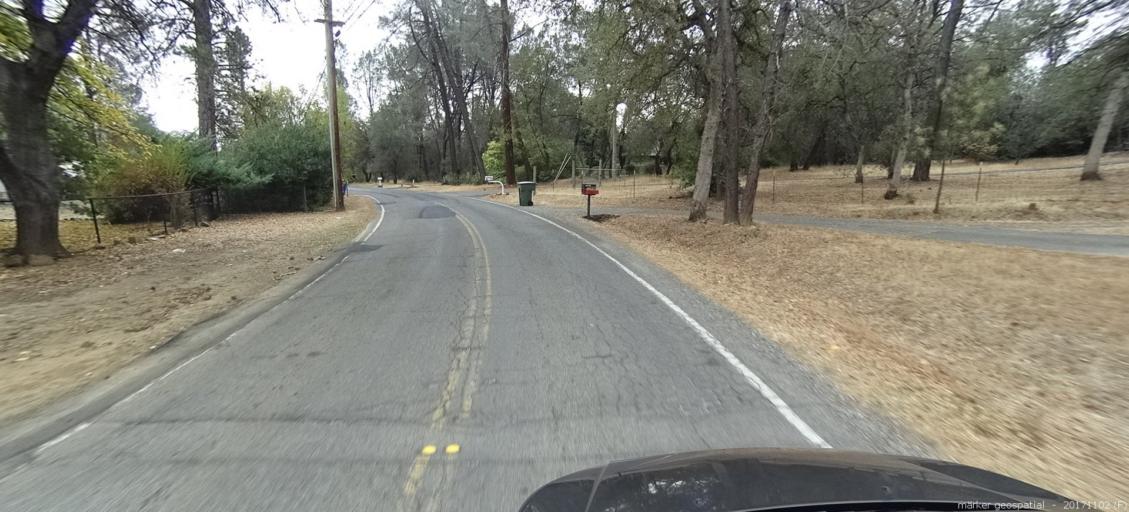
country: US
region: California
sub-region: Shasta County
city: Redding
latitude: 40.6332
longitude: -122.4079
